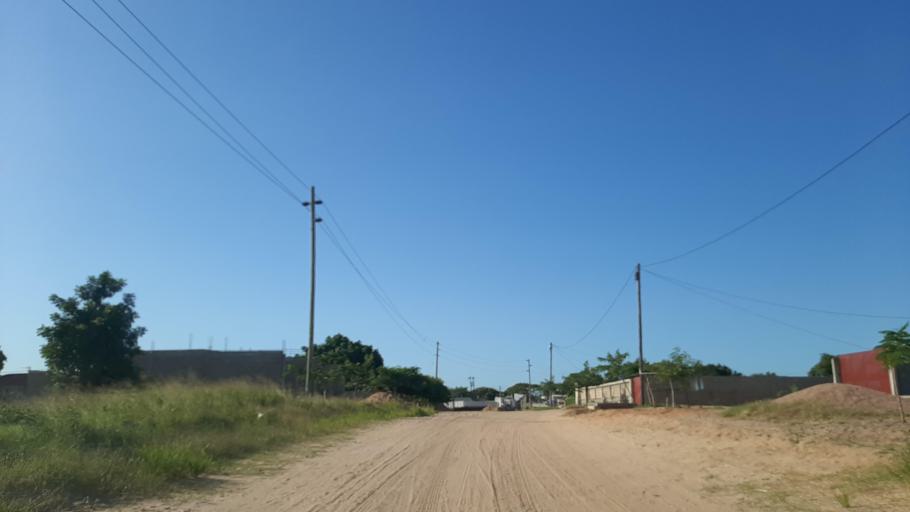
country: MZ
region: Maputo City
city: Maputo
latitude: -25.7548
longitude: 32.5501
